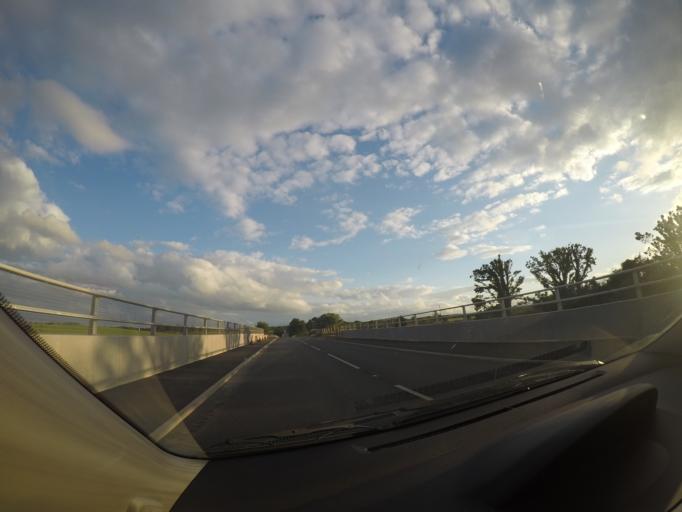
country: GB
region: England
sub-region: North Yorkshire
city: Catterick
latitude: 54.3862
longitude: -1.6547
